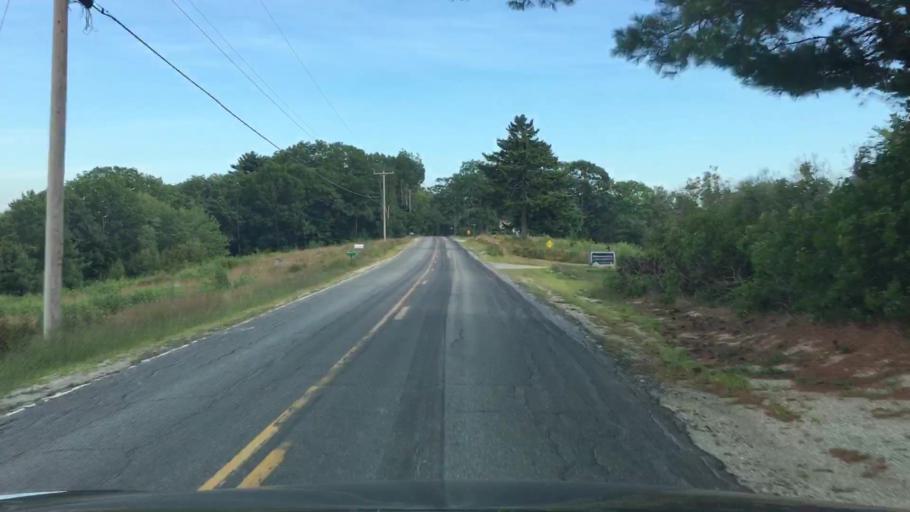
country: US
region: Maine
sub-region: Hancock County
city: Surry
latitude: 44.5140
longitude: -68.6021
